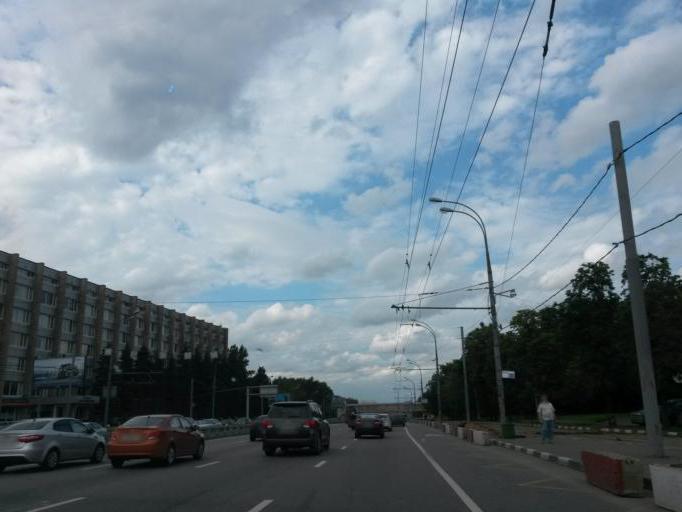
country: RU
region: Moscow
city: Nagornyy
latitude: 55.6753
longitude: 37.6264
